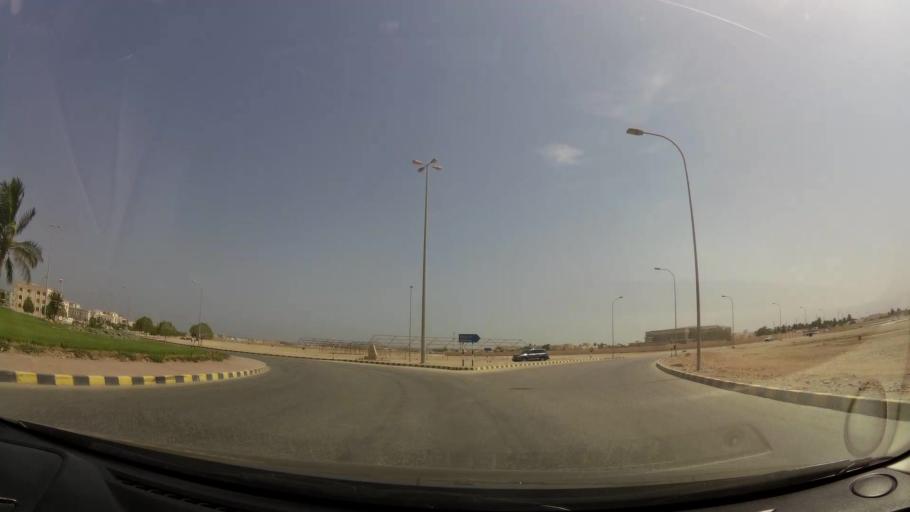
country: OM
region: Zufar
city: Salalah
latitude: 17.0507
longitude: 54.1487
